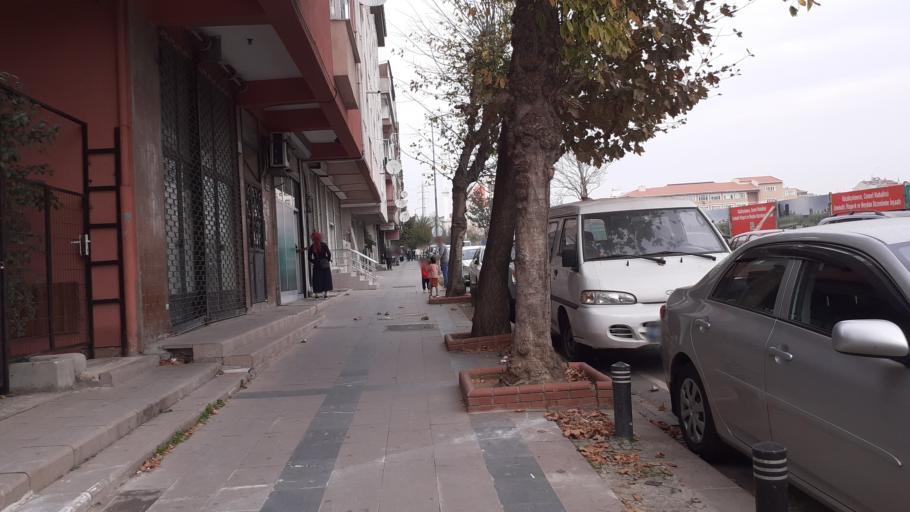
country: TR
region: Istanbul
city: Mahmutbey
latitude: 40.9890
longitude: 28.7831
